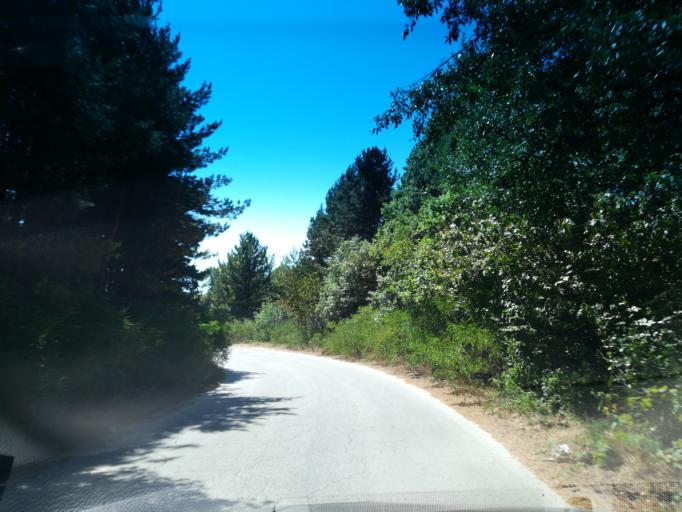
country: BG
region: Pazardzhik
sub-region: Obshtina Strelcha
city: Strelcha
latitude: 42.5394
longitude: 24.3334
